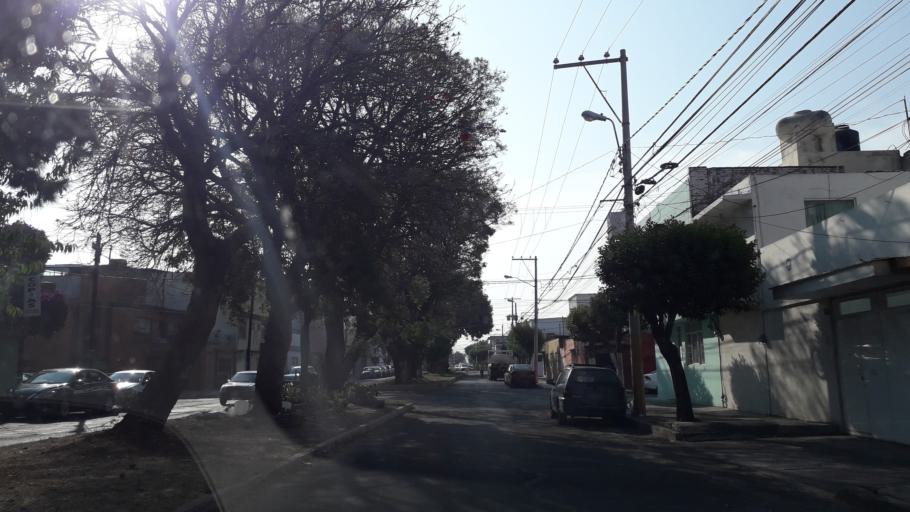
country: MX
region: Puebla
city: Puebla
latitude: 19.0419
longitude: -98.2188
